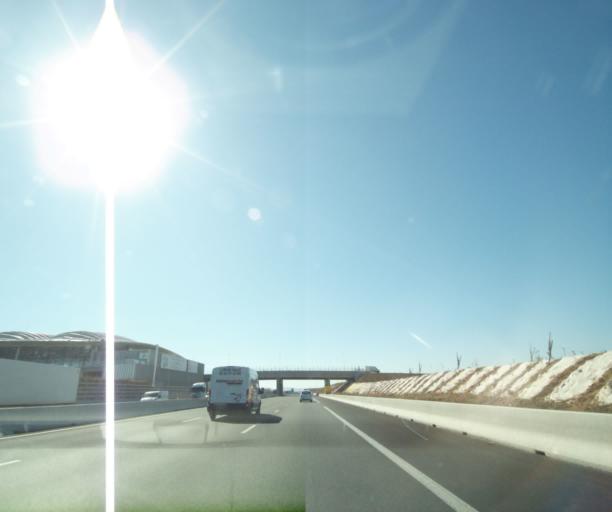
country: FR
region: Languedoc-Roussillon
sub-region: Departement de l'Herault
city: Lattes
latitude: 43.5965
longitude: 3.9250
